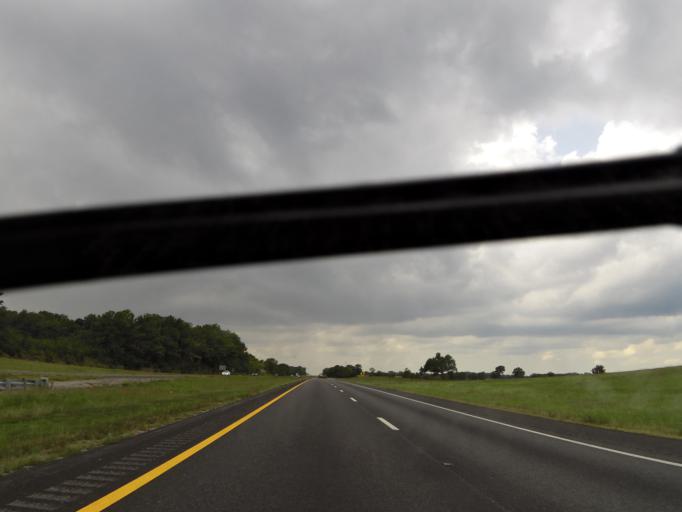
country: US
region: Tennessee
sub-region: Wilson County
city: Watertown
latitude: 36.1908
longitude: -86.1775
